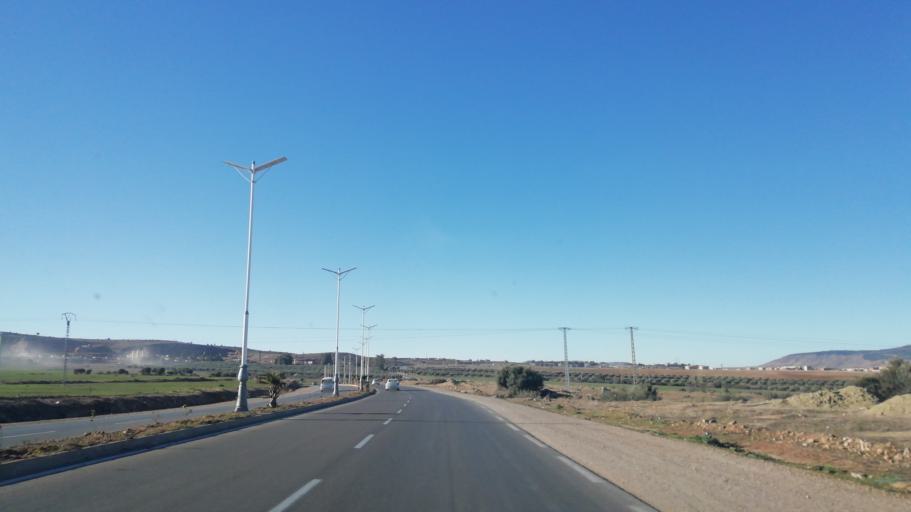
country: DZ
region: Saida
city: Saida
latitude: 34.8502
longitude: 0.1939
